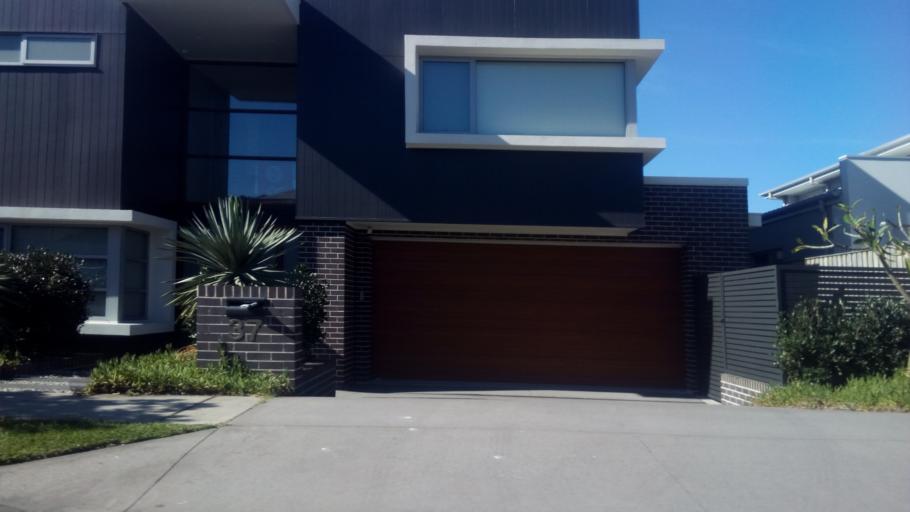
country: AU
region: New South Wales
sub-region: Wollongong
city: Bulli
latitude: -34.3246
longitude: 150.9199
